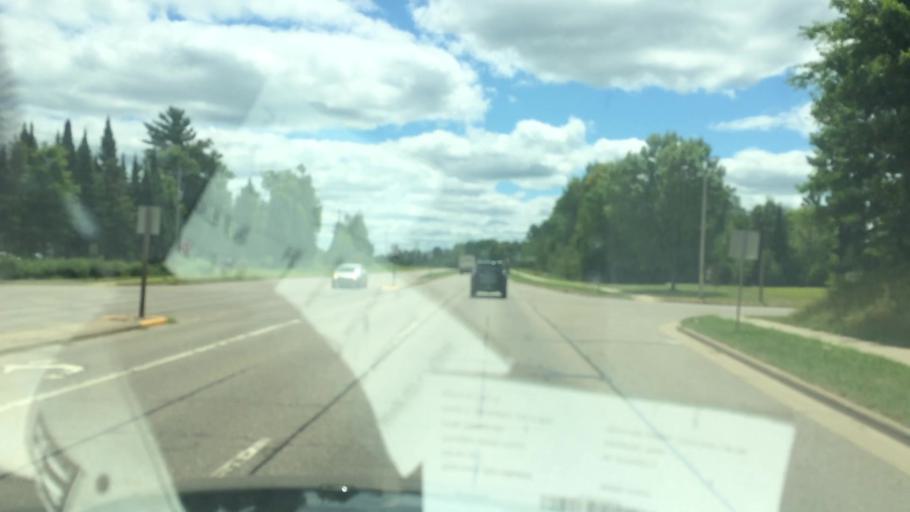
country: US
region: Wisconsin
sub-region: Oneida County
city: Rhinelander
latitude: 45.6484
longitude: -89.3821
